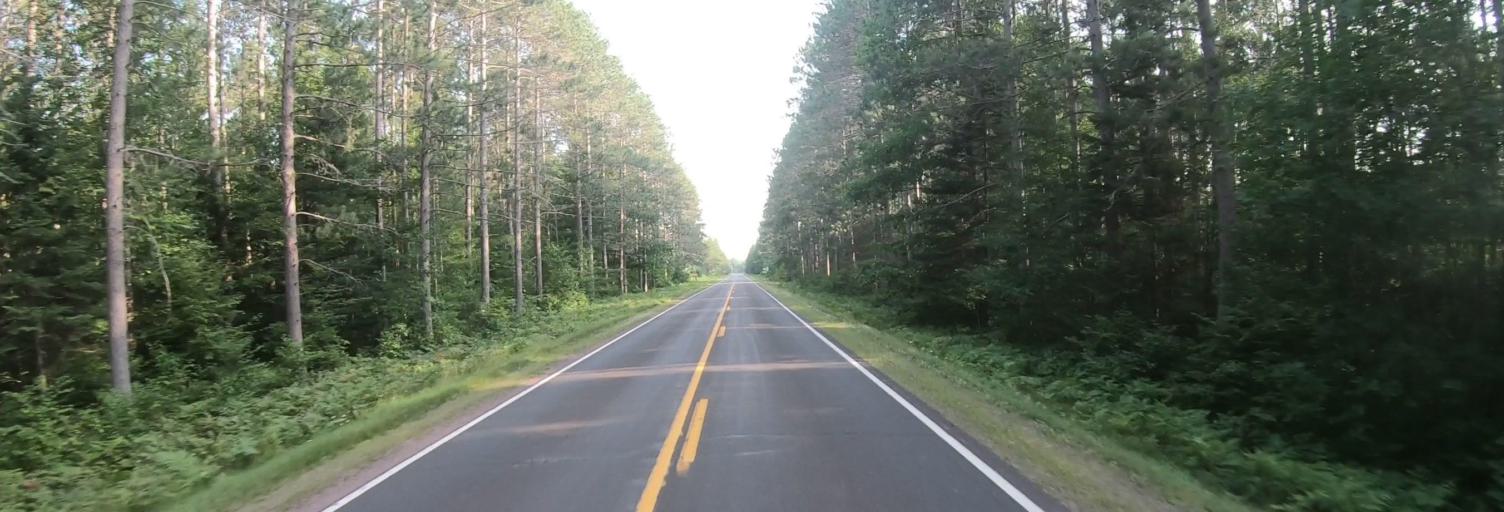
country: US
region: Wisconsin
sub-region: Ashland County
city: Ashland
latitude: 46.1769
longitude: -90.9064
